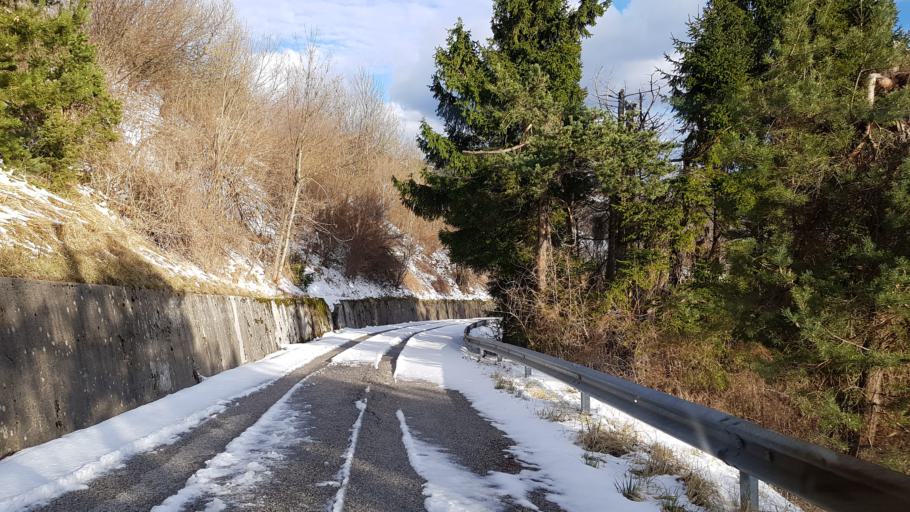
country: IT
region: Friuli Venezia Giulia
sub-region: Provincia di Udine
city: Faedis
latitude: 46.1834
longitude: 13.3892
